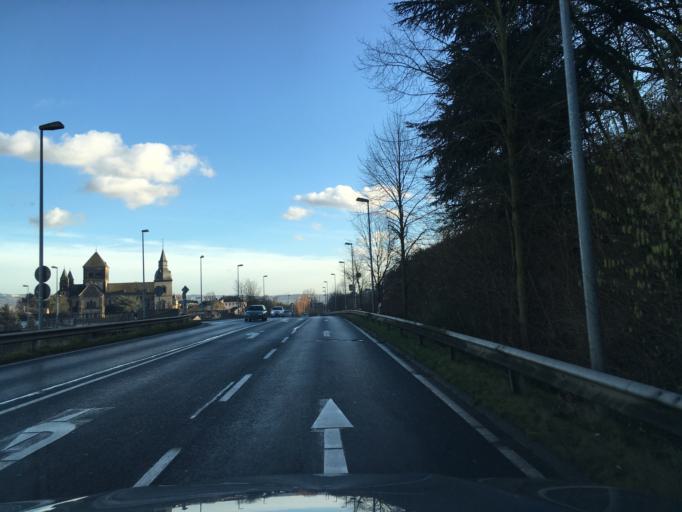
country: DE
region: Rheinland-Pfalz
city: Remagen
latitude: 50.5805
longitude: 7.2230
